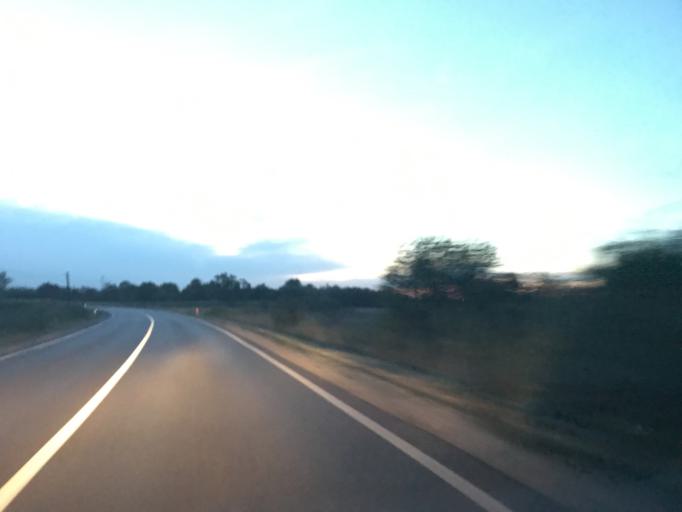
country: RS
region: Central Serbia
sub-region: Podunavski Okrug
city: Smederevo
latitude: 44.5833
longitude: 20.9836
